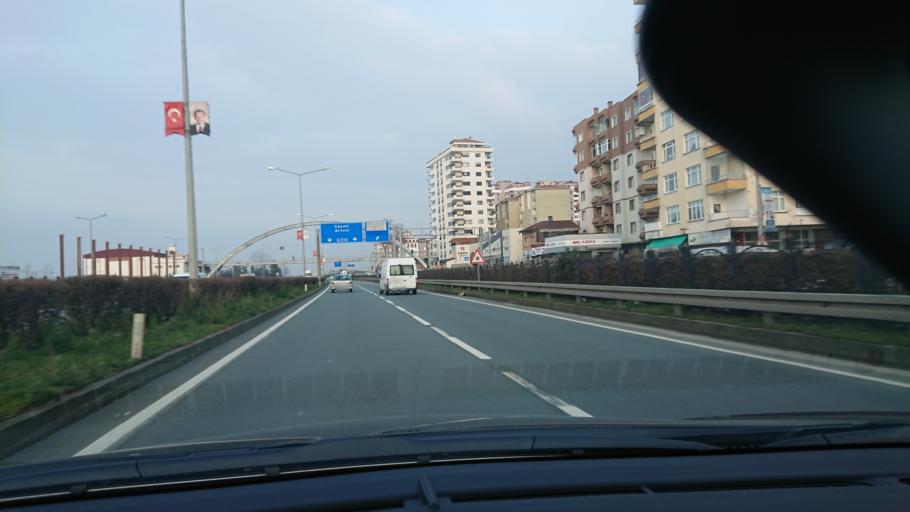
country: TR
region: Rize
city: Rize
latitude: 41.0333
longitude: 40.5577
